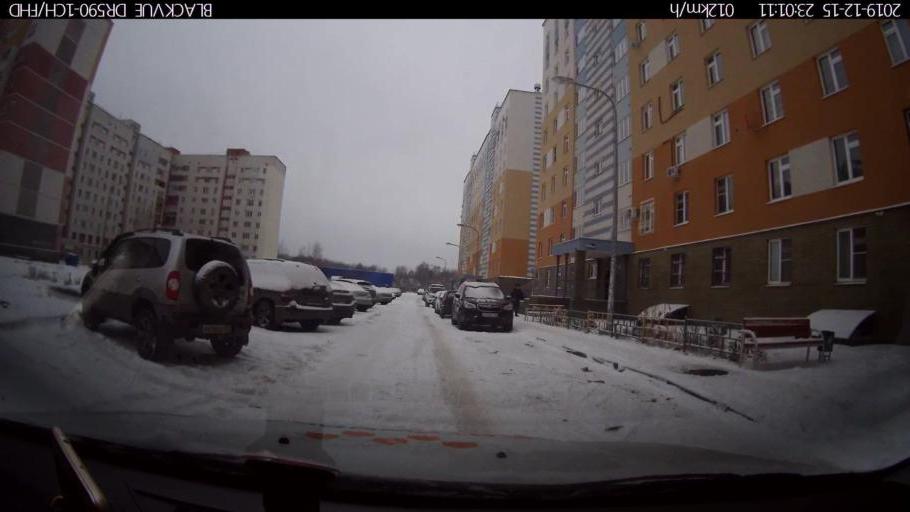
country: RU
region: Nizjnij Novgorod
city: Nizhniy Novgorod
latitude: 56.3382
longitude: 43.9123
